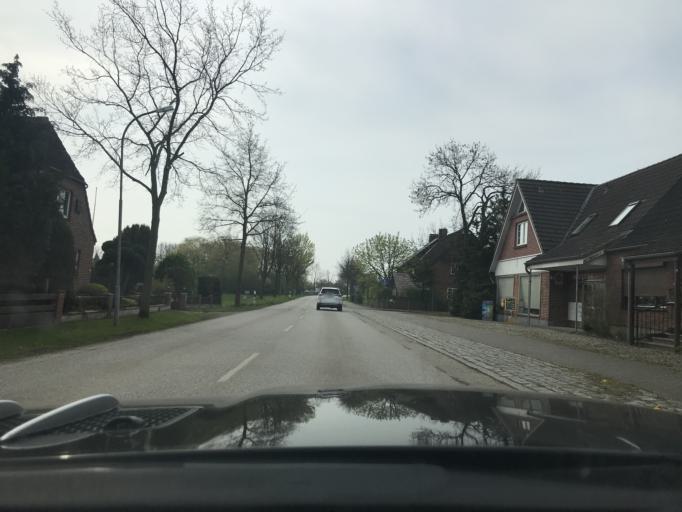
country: DE
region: Schleswig-Holstein
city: Heringsdorf
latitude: 54.2764
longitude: 11.0319
